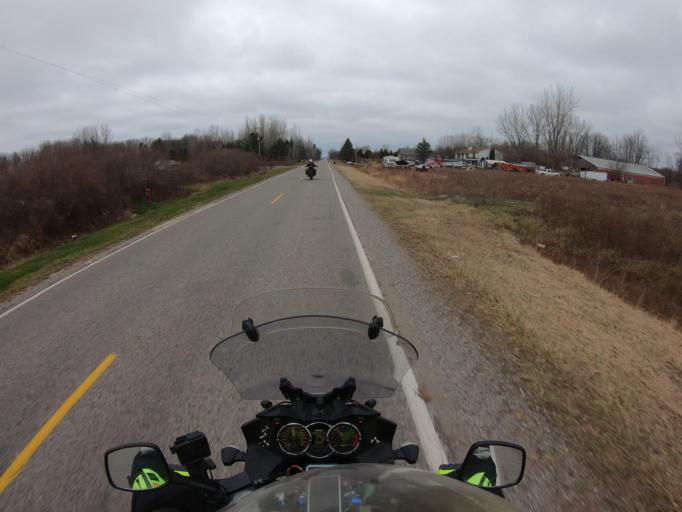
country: US
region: Michigan
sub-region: Saginaw County
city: Burt
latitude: 43.2373
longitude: -83.9864
